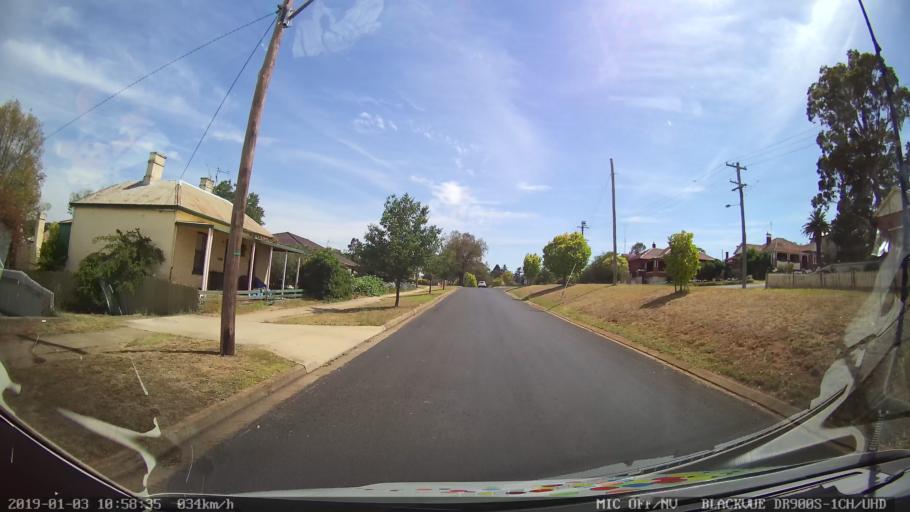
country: AU
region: New South Wales
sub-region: Young
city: Young
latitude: -34.3102
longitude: 148.2963
